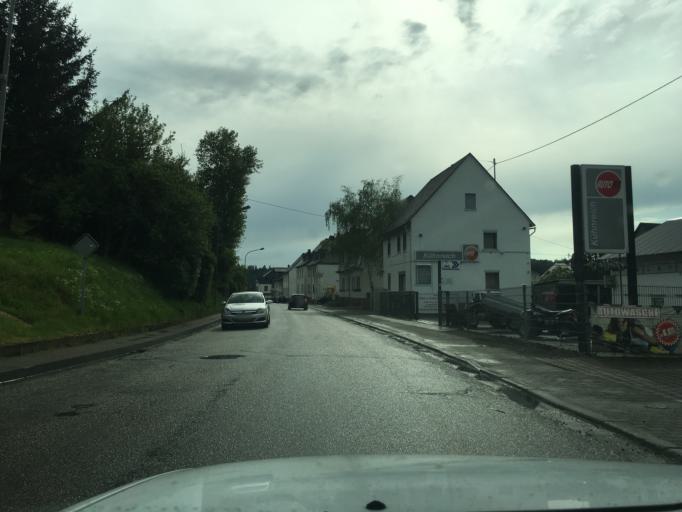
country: DE
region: Rheinland-Pfalz
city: Gemunden
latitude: 49.8969
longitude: 7.4829
